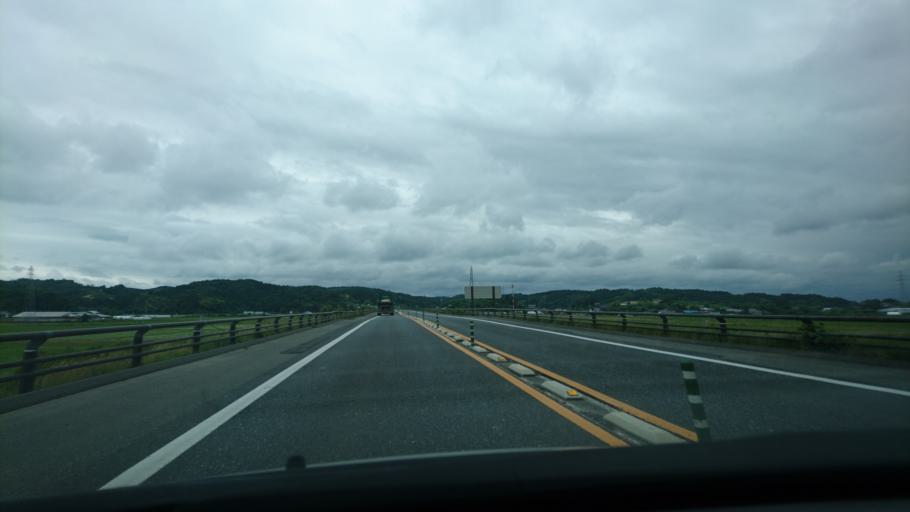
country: JP
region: Miyagi
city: Wakuya
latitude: 38.6565
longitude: 141.2646
